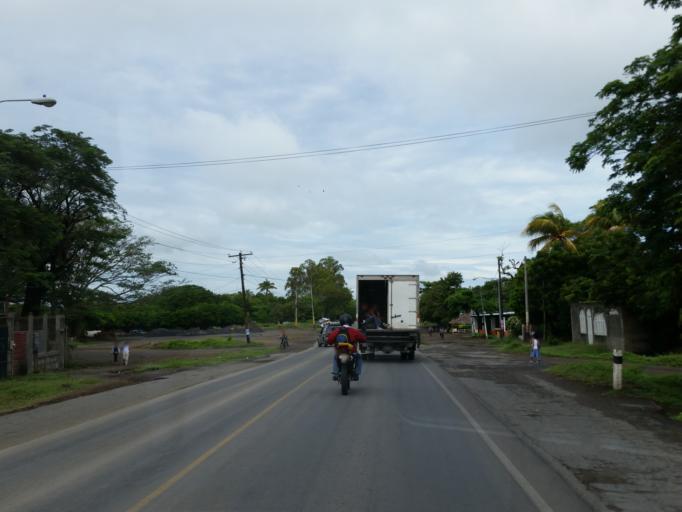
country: NI
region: Leon
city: Nagarote
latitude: 12.2711
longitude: -86.5612
